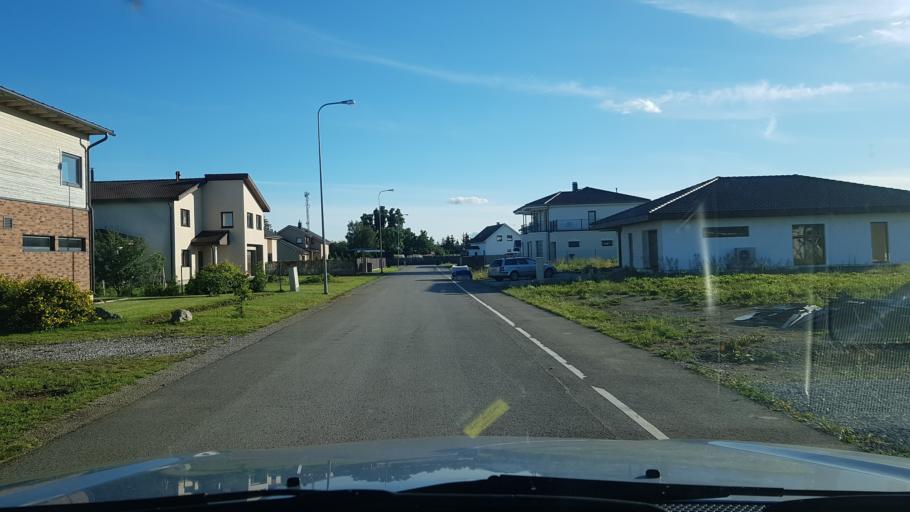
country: EE
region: Harju
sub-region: Rae vald
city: Jueri
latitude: 59.3850
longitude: 24.8442
